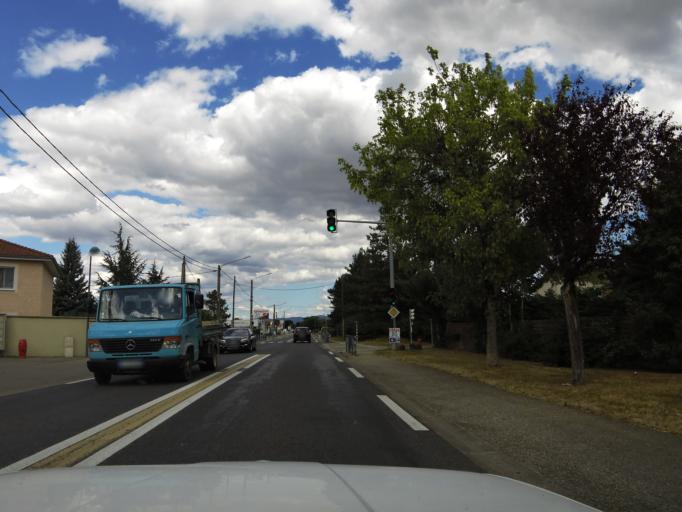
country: FR
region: Rhone-Alpes
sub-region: Departement de l'Ain
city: Loyettes
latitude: 45.7774
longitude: 5.2104
